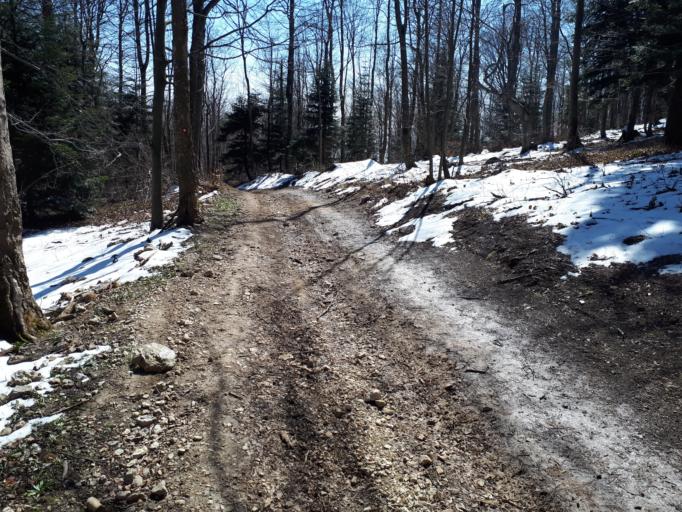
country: HR
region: Varazdinska
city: Ivanec
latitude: 46.1799
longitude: 16.1351
